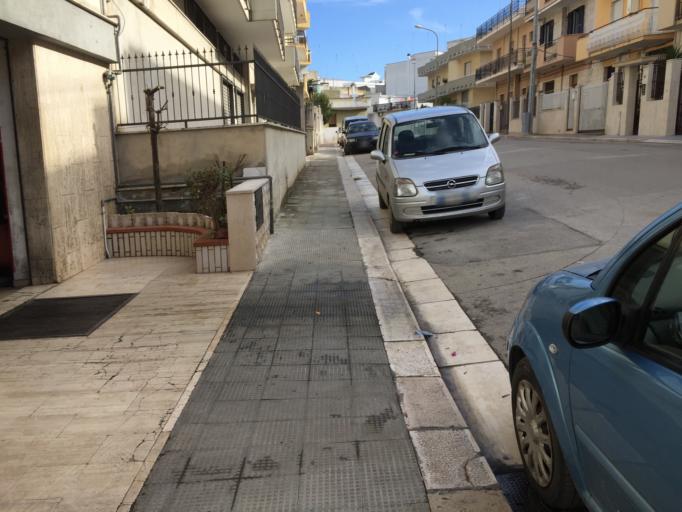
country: IT
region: Apulia
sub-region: Provincia di Barletta - Andria - Trani
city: Andria
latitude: 41.2193
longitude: 16.3015
